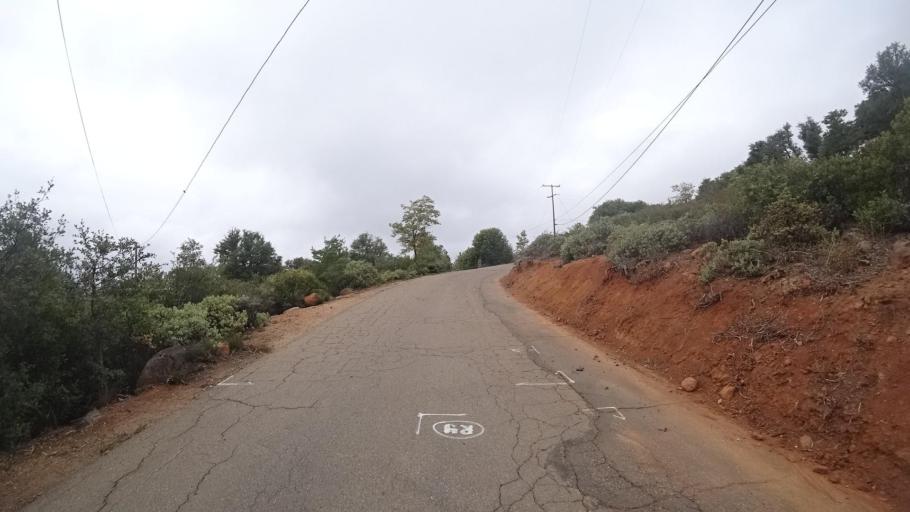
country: US
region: California
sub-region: San Diego County
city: Julian
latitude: 33.0444
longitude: -116.6308
